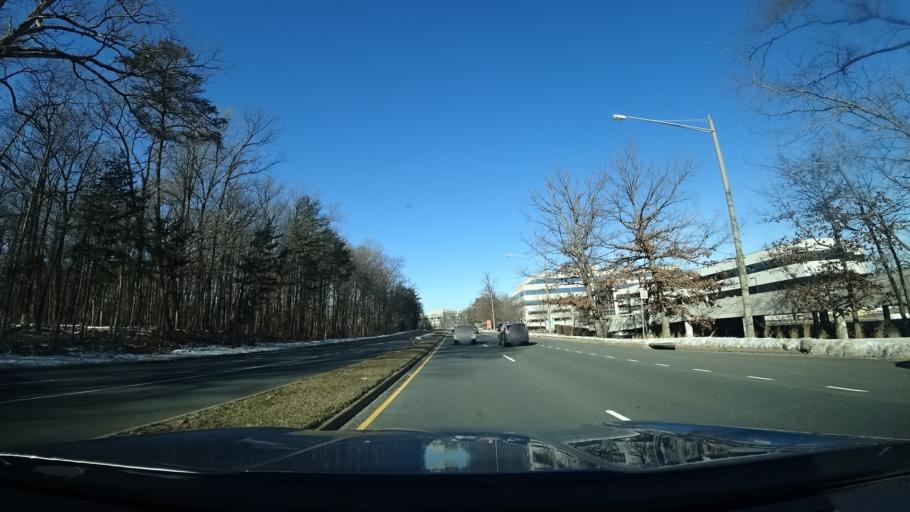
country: US
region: Virginia
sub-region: Fairfax County
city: Herndon
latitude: 38.9498
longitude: -77.3663
